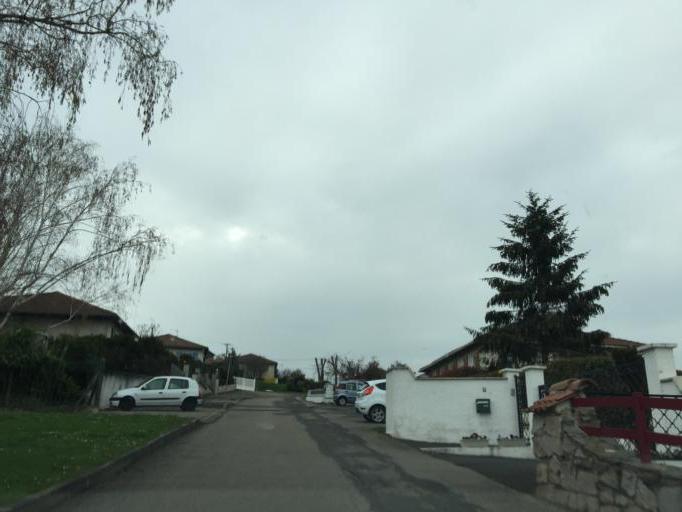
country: FR
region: Rhone-Alpes
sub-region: Departement de la Loire
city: Saint-Chamond
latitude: 45.4872
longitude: 4.5004
